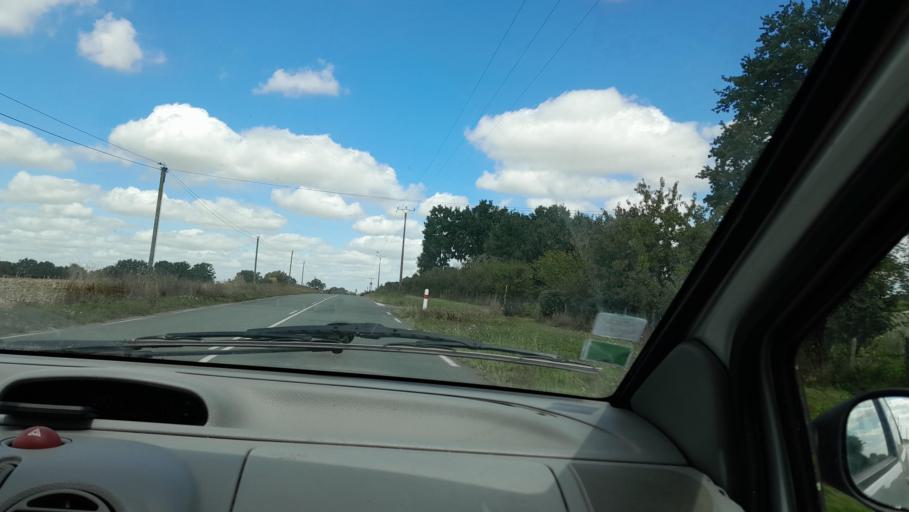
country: FR
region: Pays de la Loire
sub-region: Departement de la Mayenne
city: Ballots
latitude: 47.9304
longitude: -1.0756
